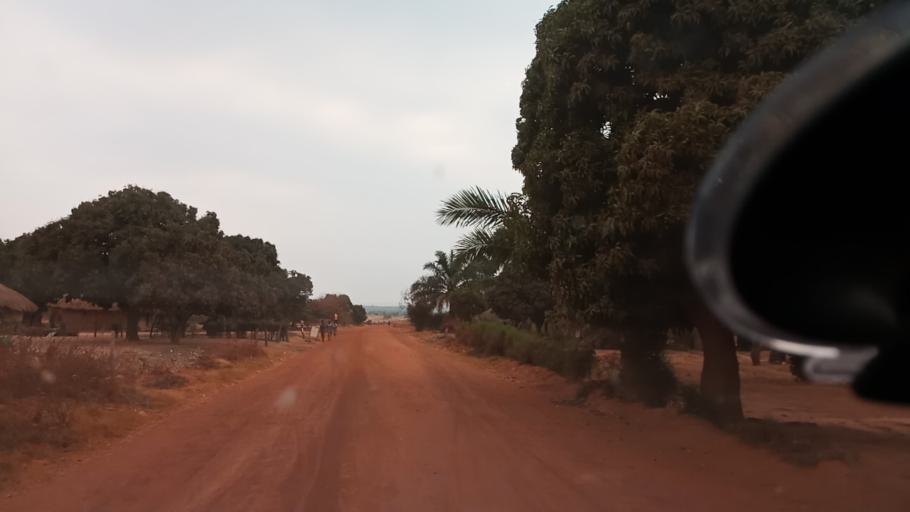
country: ZM
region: Luapula
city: Nchelenge
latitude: -9.2771
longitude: 28.3232
